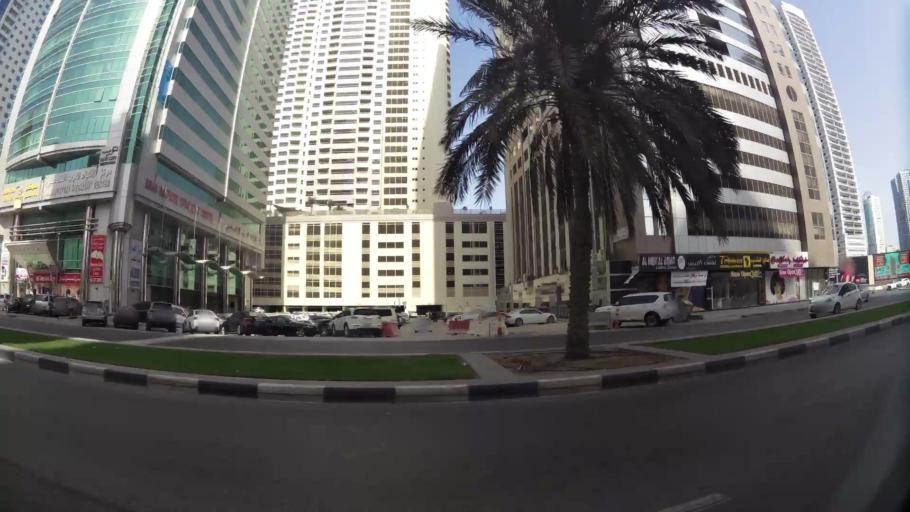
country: AE
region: Ash Shariqah
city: Sharjah
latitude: 25.3180
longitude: 55.3767
